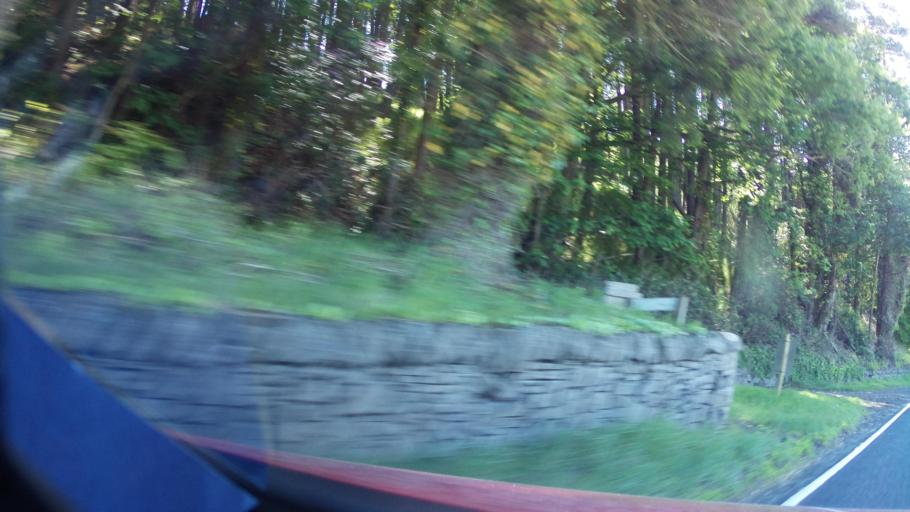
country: GB
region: Scotland
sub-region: The Scottish Borders
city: Galashiels
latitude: 55.7153
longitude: -2.8840
